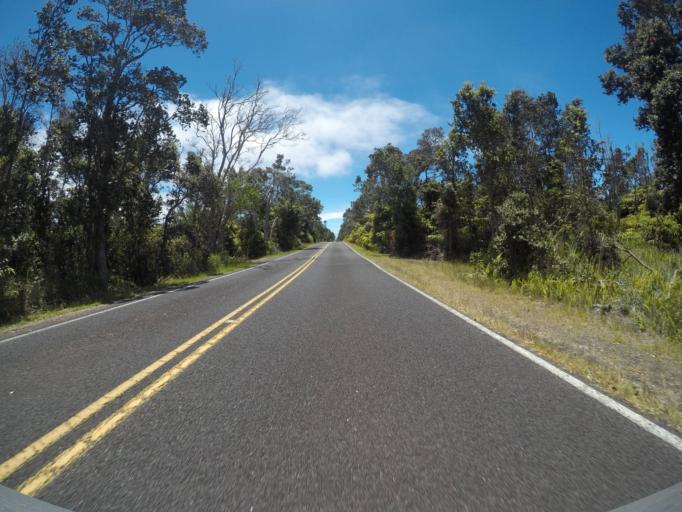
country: US
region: Hawaii
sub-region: Hawaii County
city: Volcano
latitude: 19.3662
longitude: -155.2201
